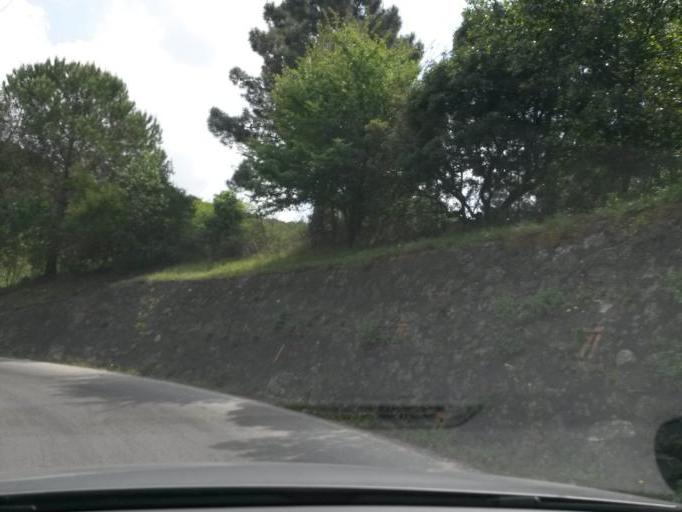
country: IT
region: Tuscany
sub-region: Provincia di Livorno
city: Portoferraio
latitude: 42.7970
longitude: 10.3297
